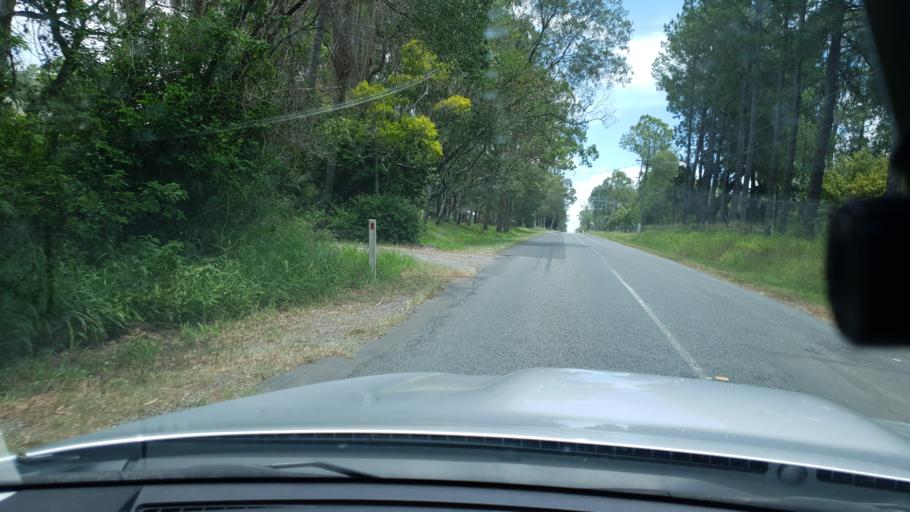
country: AU
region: Queensland
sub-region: Logan
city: North Maclean
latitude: -27.7726
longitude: 152.9938
